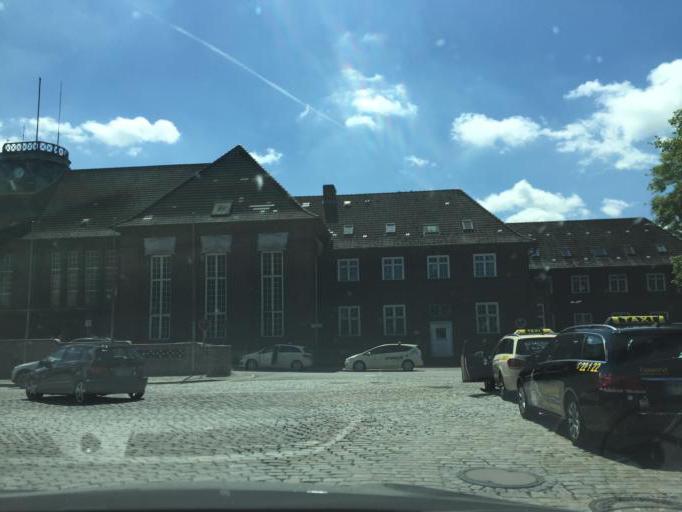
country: DE
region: Schleswig-Holstein
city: Flensburg
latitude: 54.7752
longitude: 9.4366
